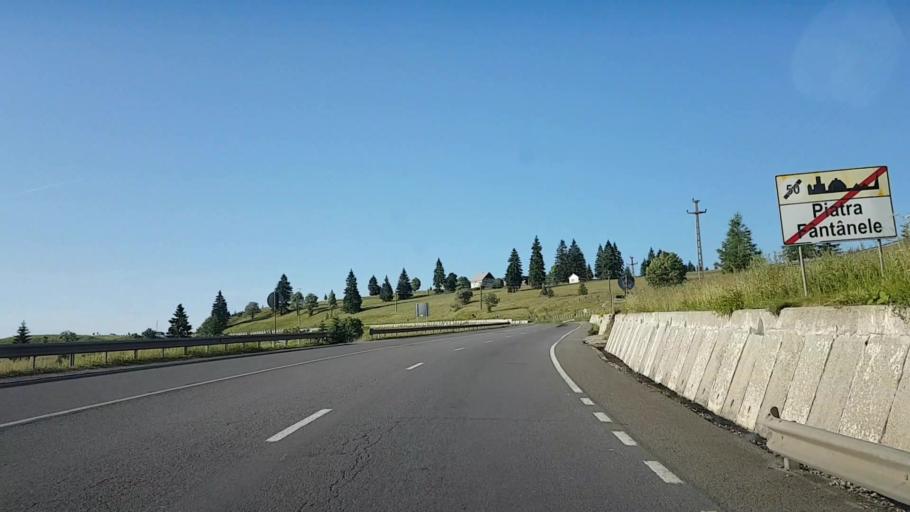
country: RO
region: Bistrita-Nasaud
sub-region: Comuna Lunca Ilvei
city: Lunca Ilvei
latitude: 47.2431
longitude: 25.0193
